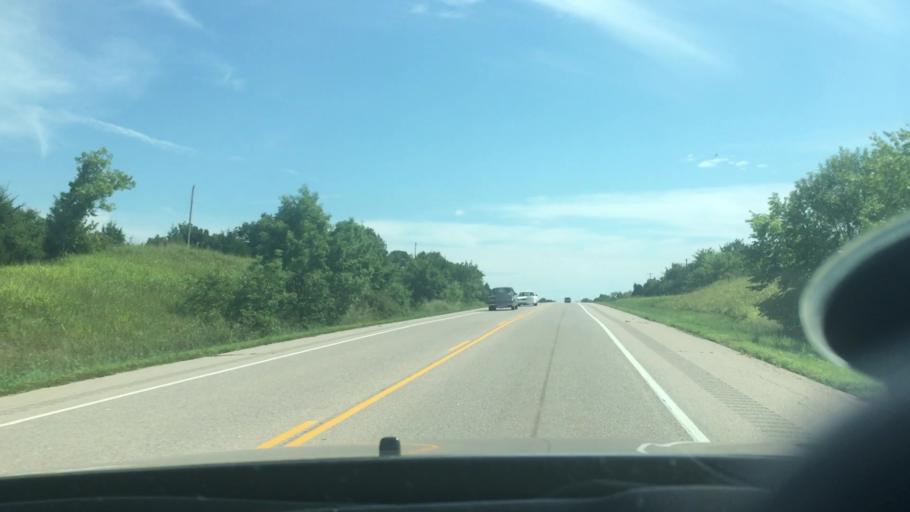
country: US
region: Oklahoma
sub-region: Seminole County
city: Konawa
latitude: 35.0016
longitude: -96.6789
